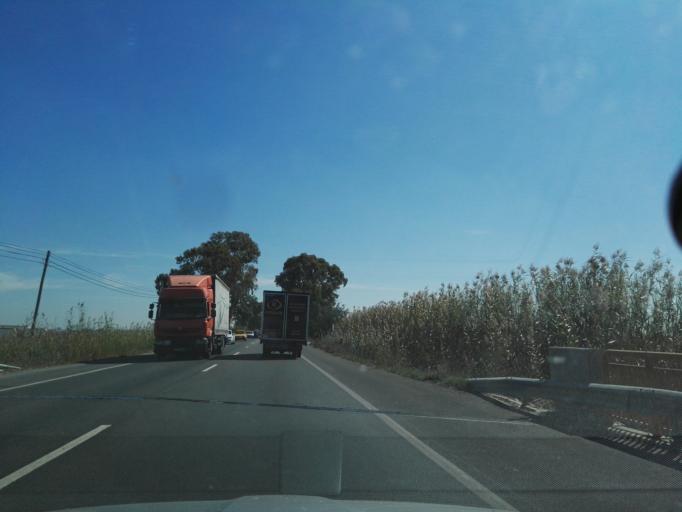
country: PT
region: Lisbon
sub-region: Vila Franca de Xira
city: Vila Franca de Xira
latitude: 38.9387
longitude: -8.9347
